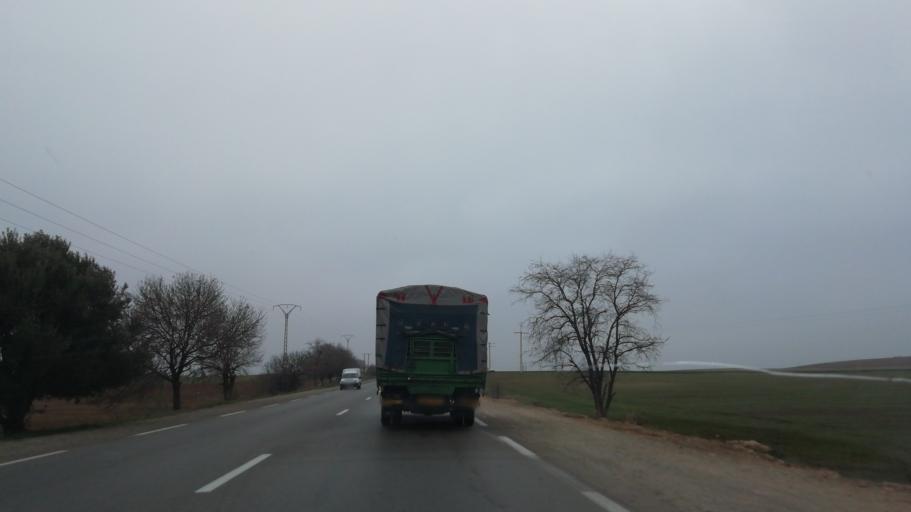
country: DZ
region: Mascara
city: Mascara
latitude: 35.3172
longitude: 0.3737
